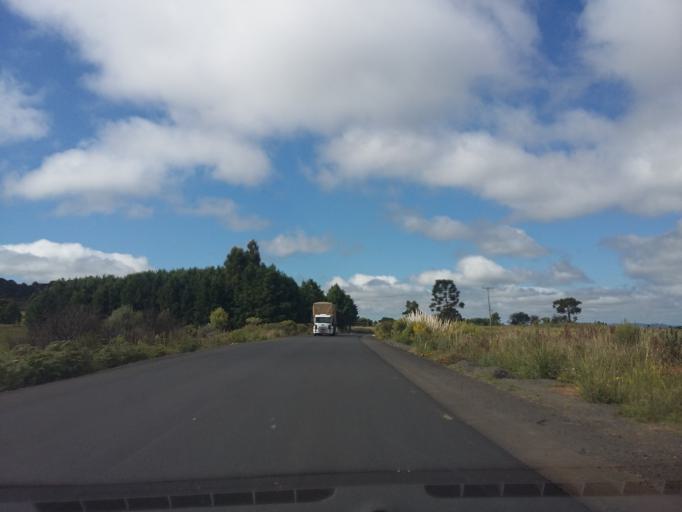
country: BR
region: Santa Catarina
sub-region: Sao Joaquim
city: Sao Joaquim
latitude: -28.0406
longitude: -50.0732
